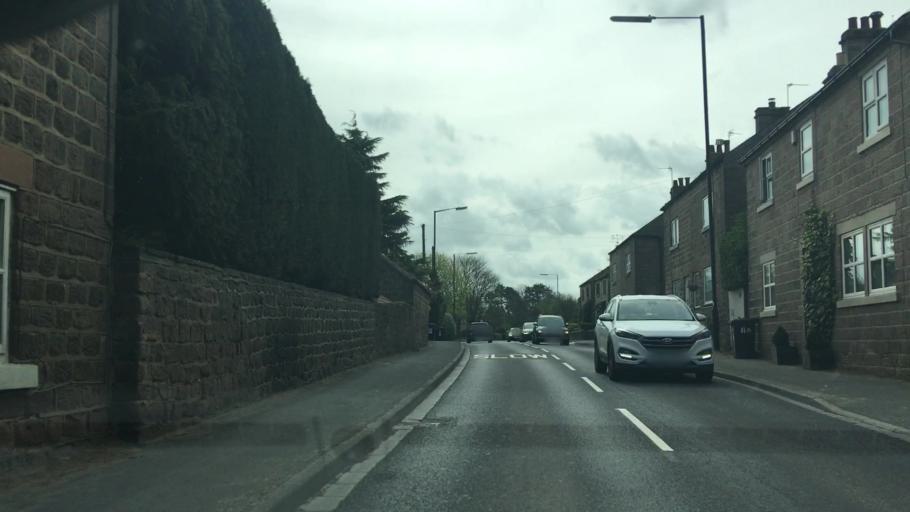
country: GB
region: England
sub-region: City and Borough of Leeds
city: Collingham
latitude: 53.9523
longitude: -1.4460
